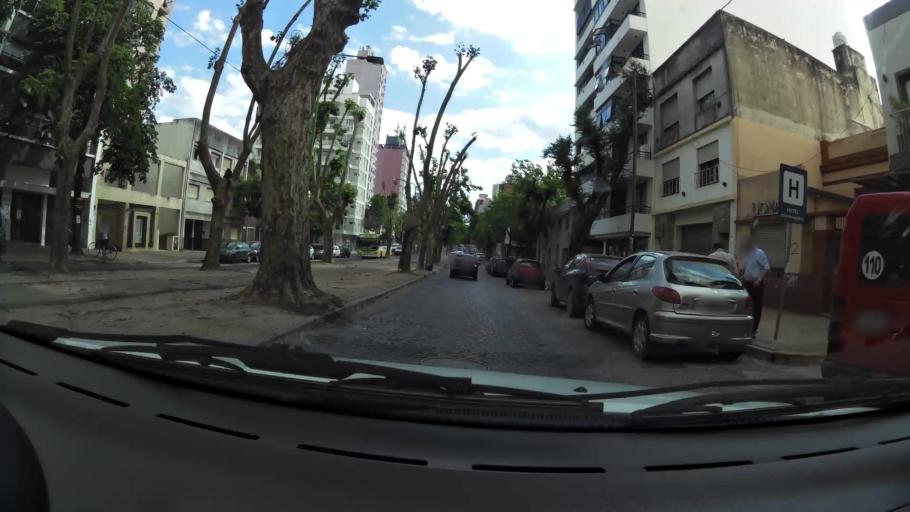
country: AR
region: Buenos Aires
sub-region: Partido de La Plata
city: La Plata
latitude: -34.9167
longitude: -57.9370
